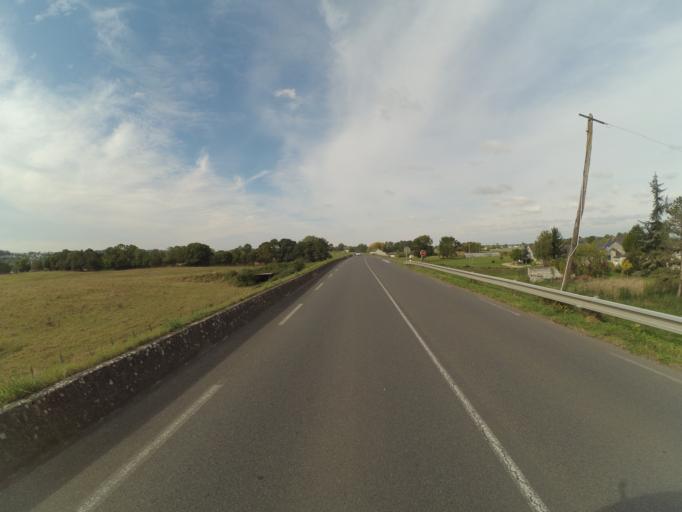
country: FR
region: Pays de la Loire
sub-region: Departement de Maine-et-Loire
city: Villebernier
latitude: 47.2556
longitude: -0.0376
